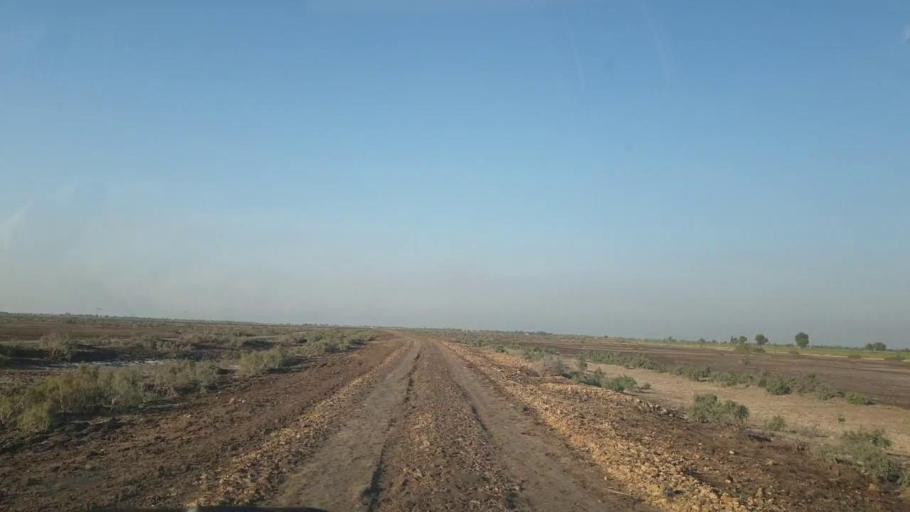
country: PK
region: Sindh
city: Mirpur Khas
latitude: 25.4377
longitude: 69.1011
